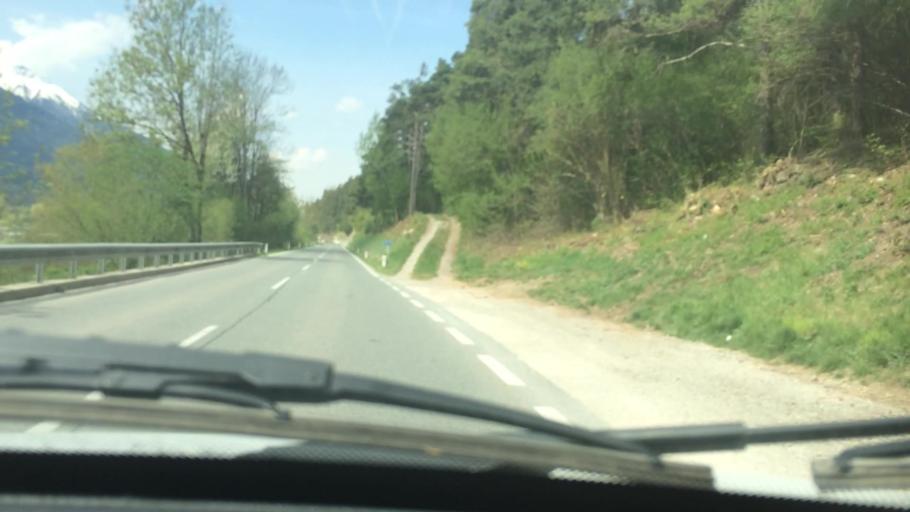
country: AT
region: Tyrol
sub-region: Politischer Bezirk Innsbruck Land
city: Zirl
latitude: 47.2797
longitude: 11.2208
